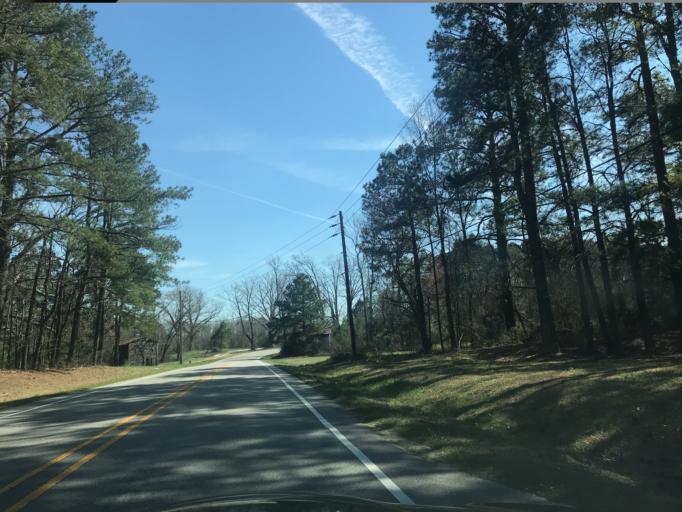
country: US
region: North Carolina
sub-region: Wake County
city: Fuquay-Varina
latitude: 35.5755
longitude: -78.7701
